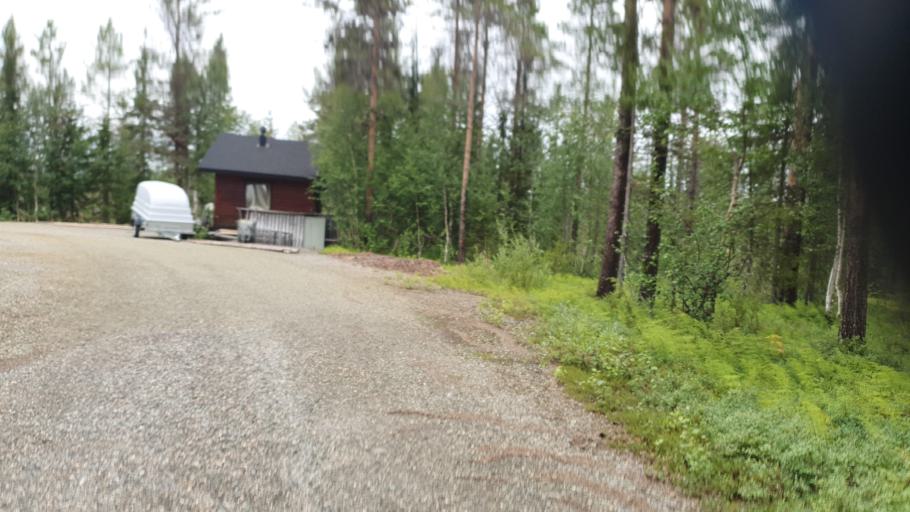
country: FI
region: Lapland
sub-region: Tunturi-Lappi
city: Kolari
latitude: 67.6134
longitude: 24.1389
